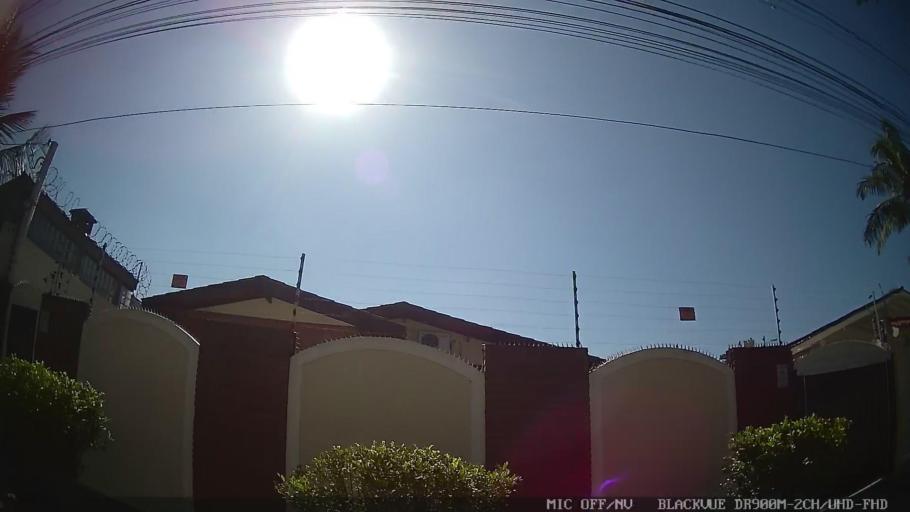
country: BR
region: Sao Paulo
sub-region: Guaruja
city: Guaruja
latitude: -23.9847
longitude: -46.2095
